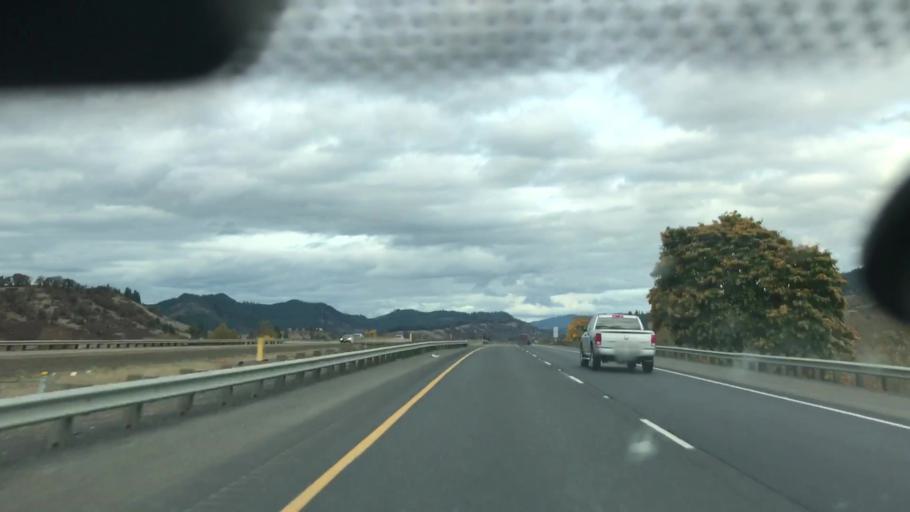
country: US
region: Oregon
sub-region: Douglas County
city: Yoncalla
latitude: 43.5676
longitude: -123.2752
